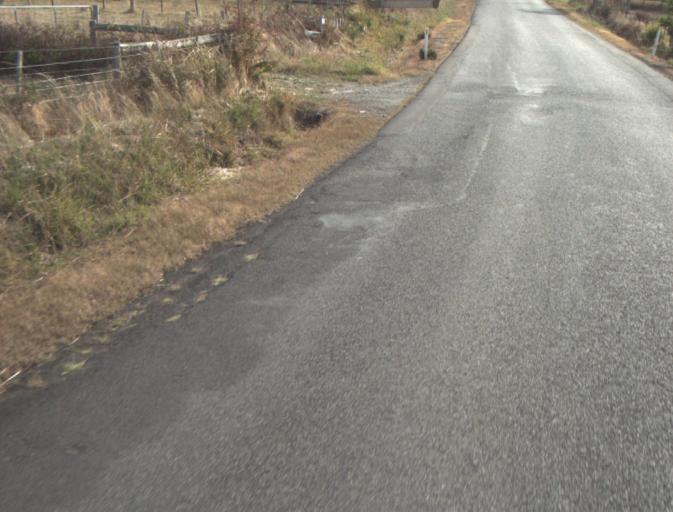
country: AU
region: Tasmania
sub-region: Launceston
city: Mayfield
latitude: -41.2380
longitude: 147.1600
